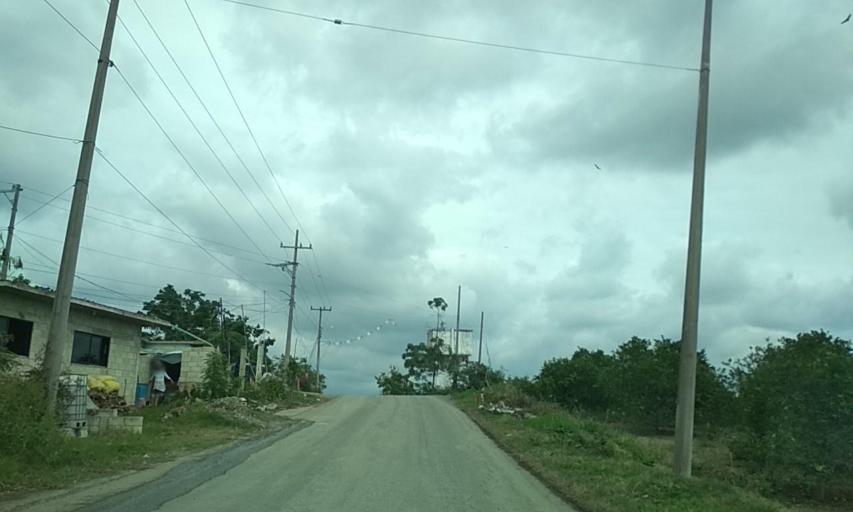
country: MX
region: Veracruz
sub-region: Papantla
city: El Chote
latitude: 20.3571
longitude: -97.3420
